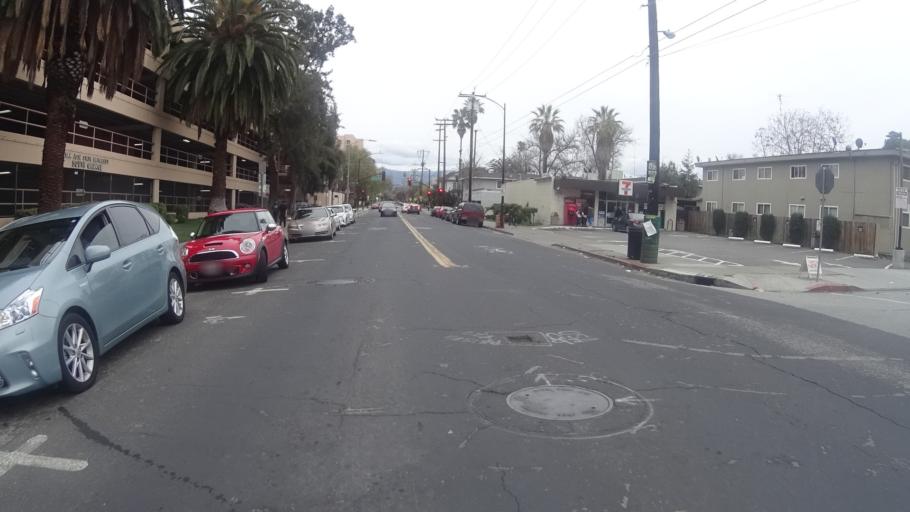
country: US
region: California
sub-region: Santa Clara County
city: San Jose
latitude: 37.3326
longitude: -121.8807
